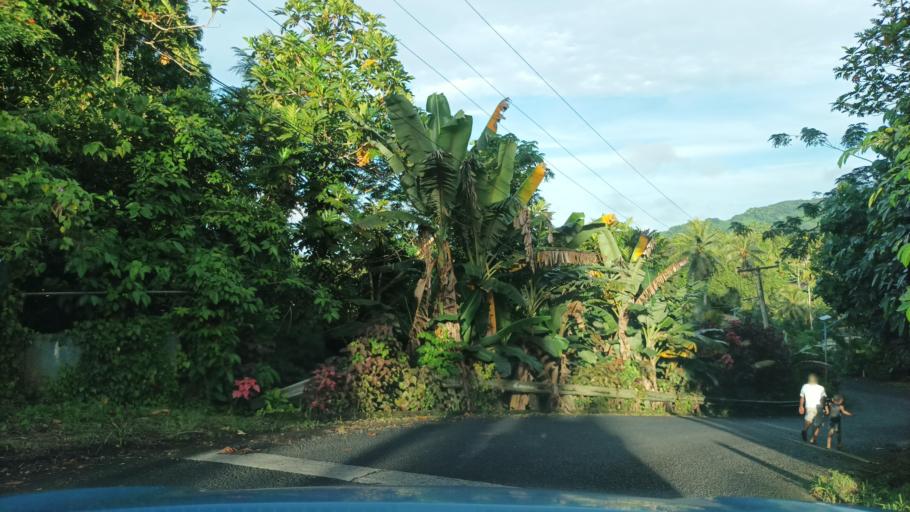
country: FM
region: Pohnpei
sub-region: Kolonia Municipality
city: Kolonia Town
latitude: 6.9669
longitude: 158.2048
